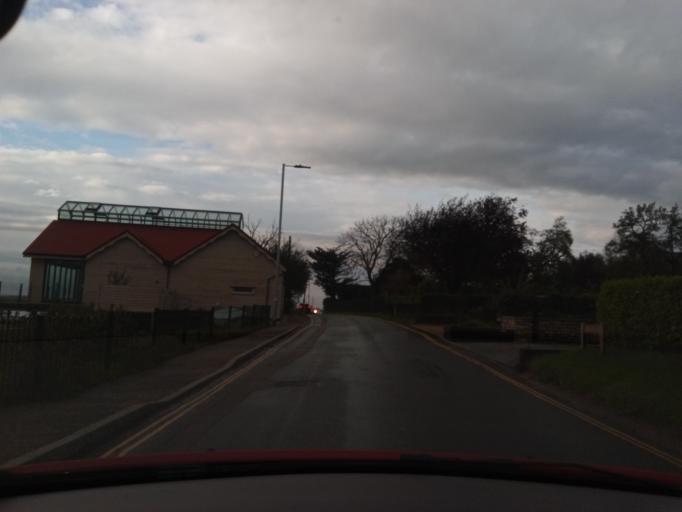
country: GB
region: England
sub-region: Essex
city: West Mersea
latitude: 51.7774
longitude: 0.8998
